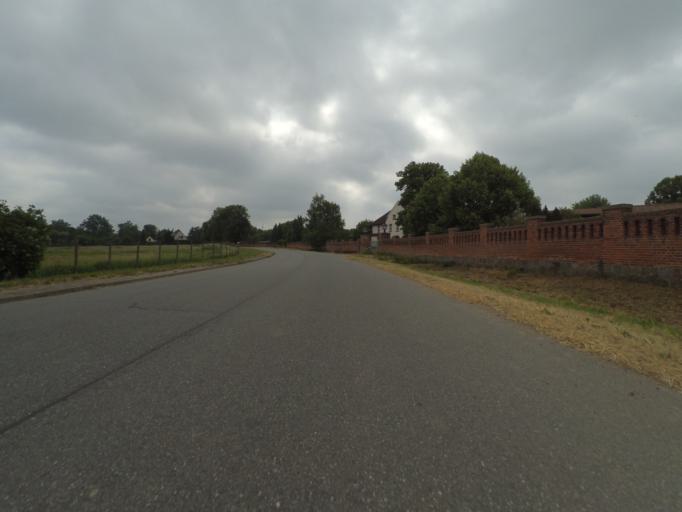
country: DE
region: Mecklenburg-Vorpommern
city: Plau am See
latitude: 53.5371
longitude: 12.2525
